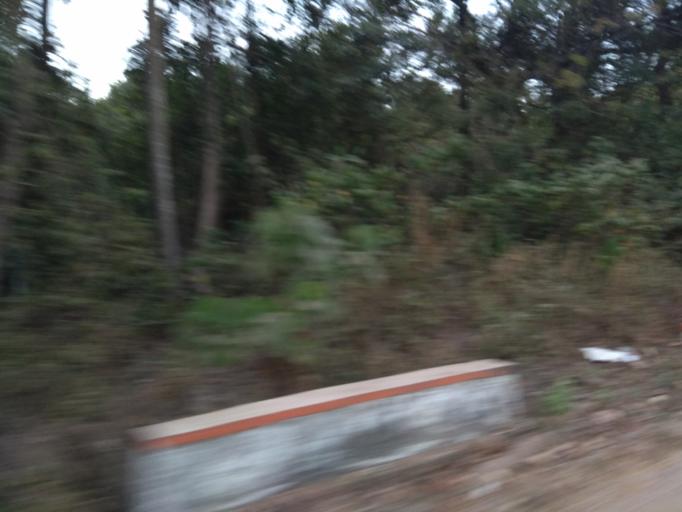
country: IN
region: Karnataka
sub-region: Dakshina Kannada
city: Mangalore
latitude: 12.9284
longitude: 74.8763
